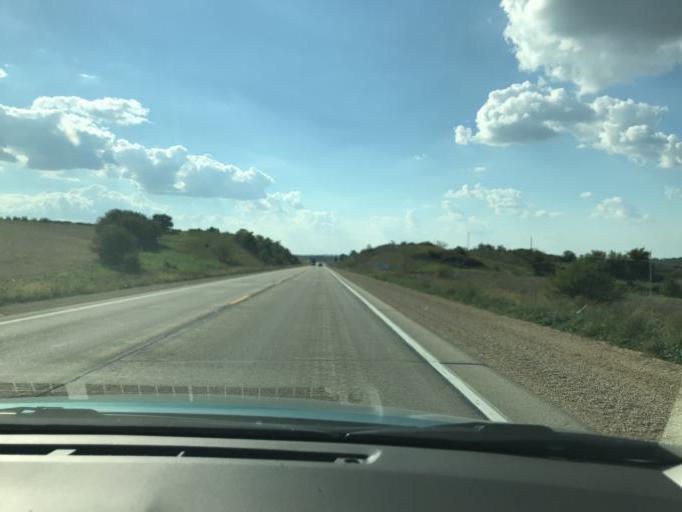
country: US
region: Wisconsin
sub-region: Green County
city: Brodhead
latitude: 42.5883
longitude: -89.4580
